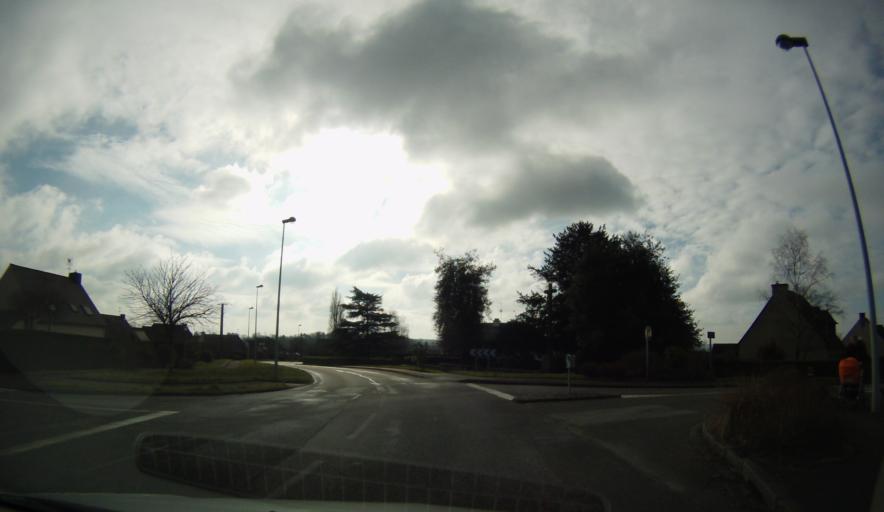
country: FR
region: Brittany
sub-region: Departement d'Ille-et-Vilaine
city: Corps-Nuds
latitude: 47.9763
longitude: -1.5860
